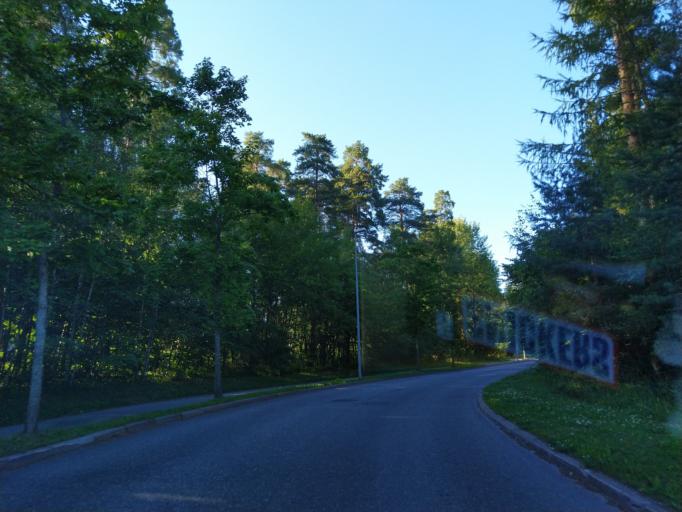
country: FI
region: Varsinais-Suomi
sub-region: Turku
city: Kaarina
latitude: 60.4440
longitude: 22.3375
